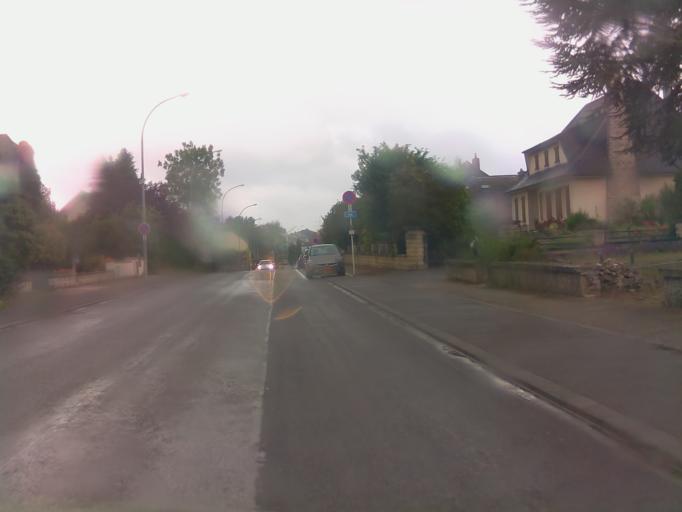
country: LU
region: Luxembourg
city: Bergem
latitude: 49.5181
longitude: 6.0679
